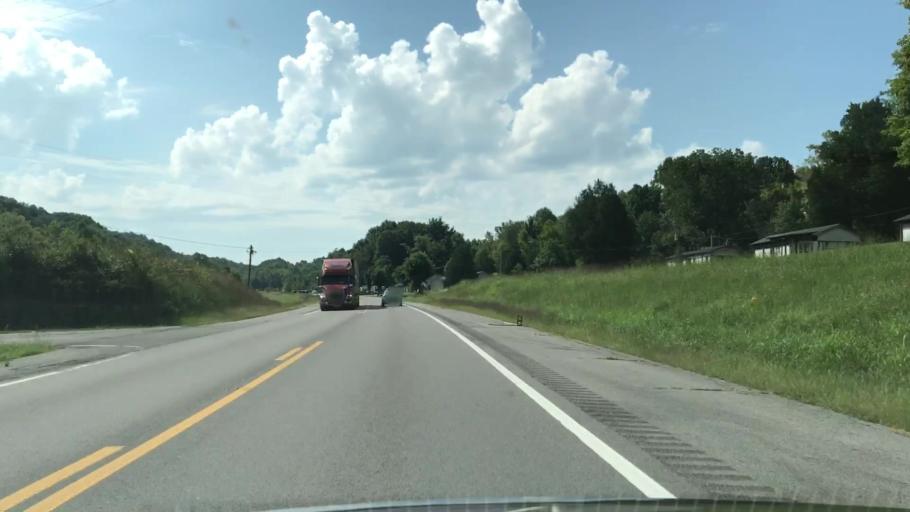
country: US
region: Tennessee
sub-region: Sumner County
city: Westmoreland
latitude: 36.6368
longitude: -86.2430
